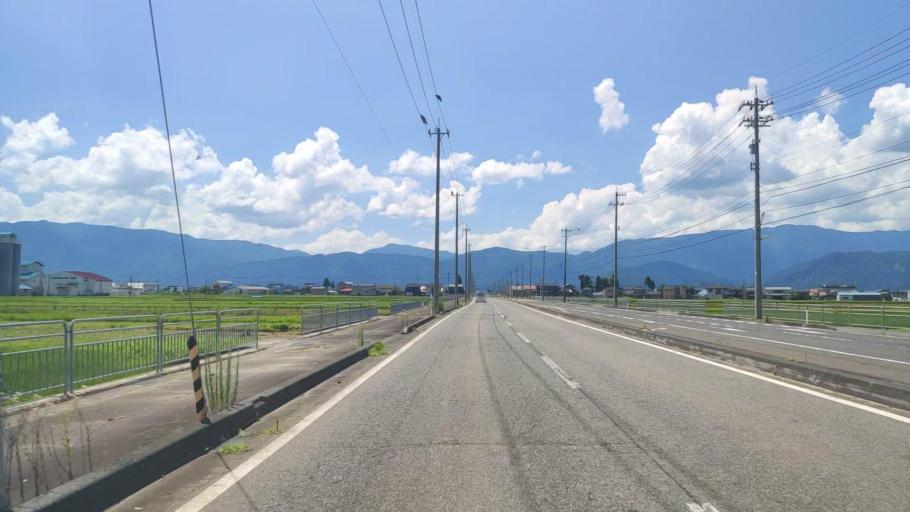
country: JP
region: Fukui
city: Ono
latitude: 35.9938
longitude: 136.5096
